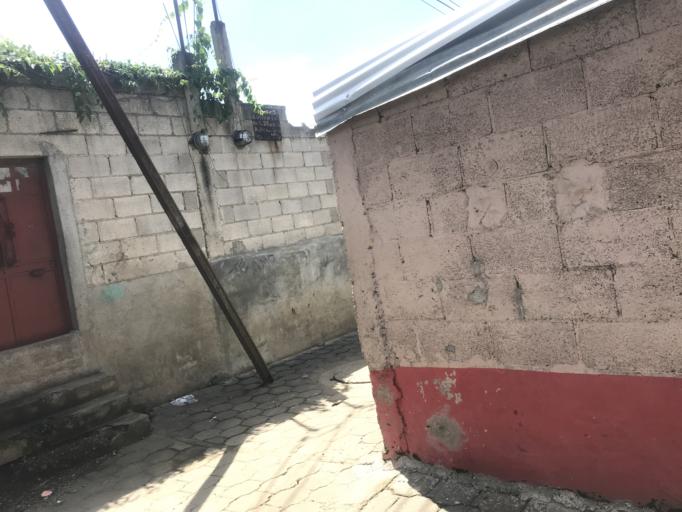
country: GT
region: Guatemala
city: Amatitlan
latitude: 14.4795
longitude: -90.6322
